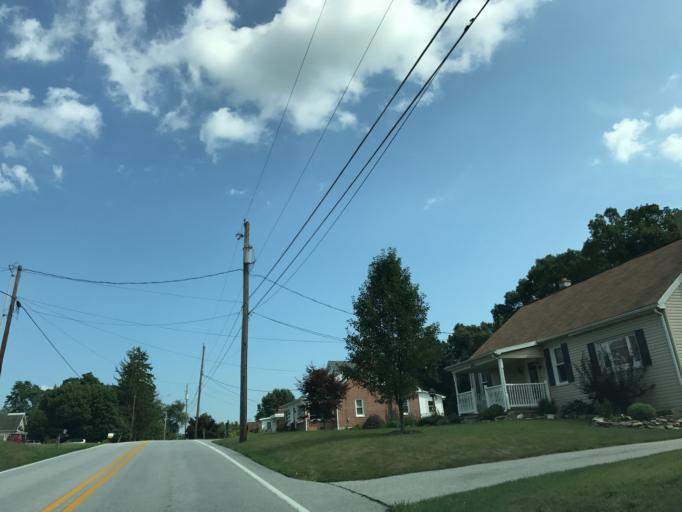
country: US
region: Pennsylvania
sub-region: Adams County
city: Mount Pleasant
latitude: 39.7545
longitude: -77.0342
